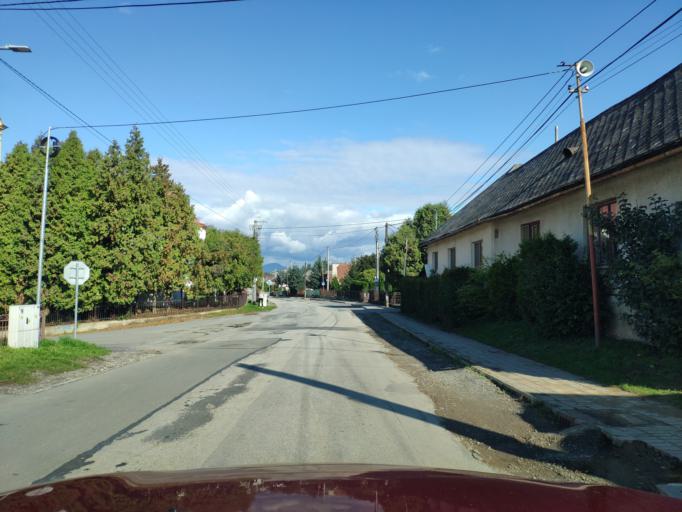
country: SK
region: Presovsky
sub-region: Okres Presov
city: Presov
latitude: 48.9167
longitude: 21.2607
